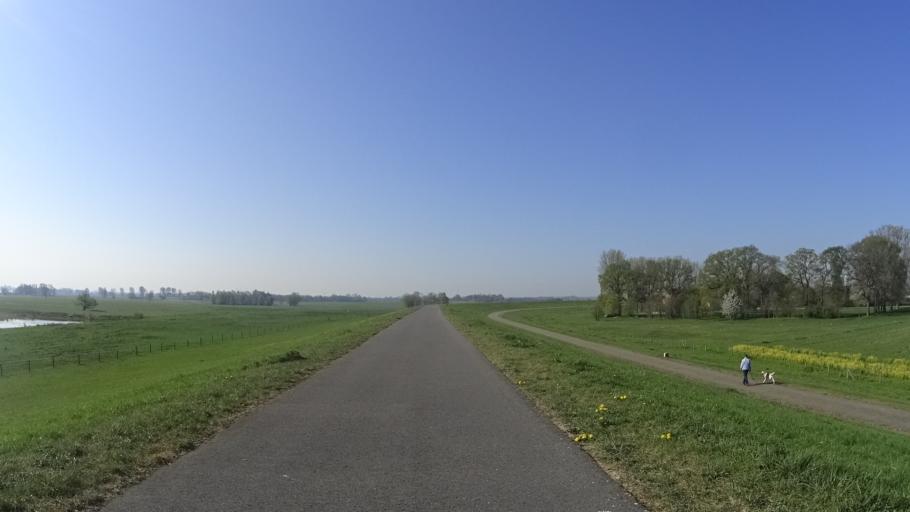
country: DE
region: North Rhine-Westphalia
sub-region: Regierungsbezirk Dusseldorf
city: Wesel
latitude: 51.6219
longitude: 6.5805
